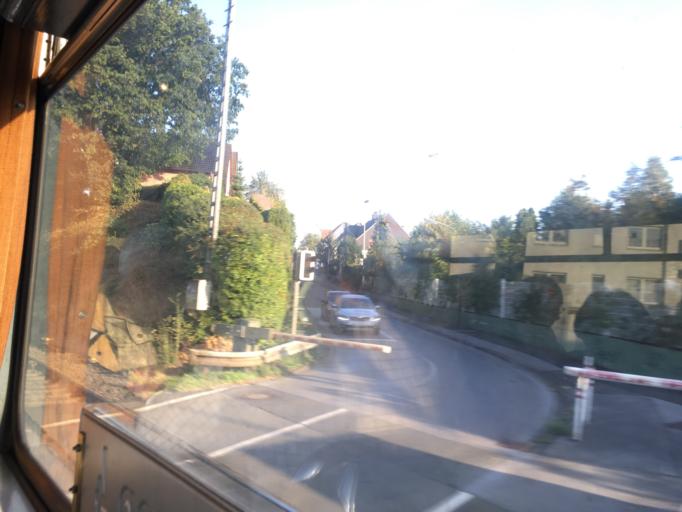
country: DE
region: North Rhine-Westphalia
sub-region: Regierungsbezirk Arnsberg
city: Frondenberg
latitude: 51.4749
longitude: 7.7108
